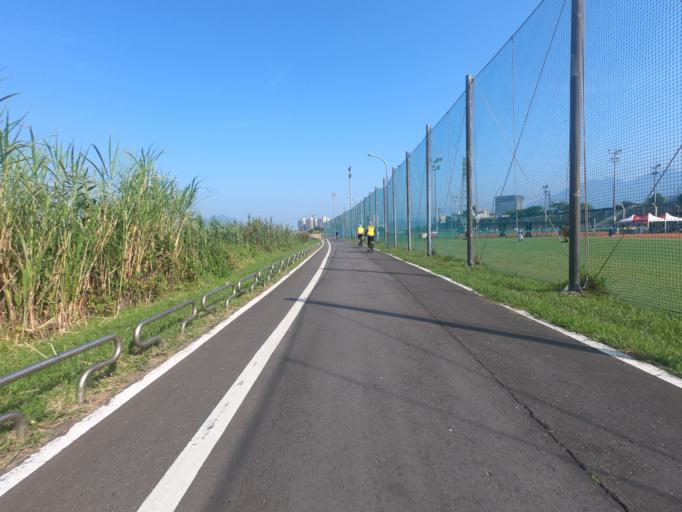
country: TW
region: Taipei
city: Taipei
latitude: 25.0936
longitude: 121.5123
